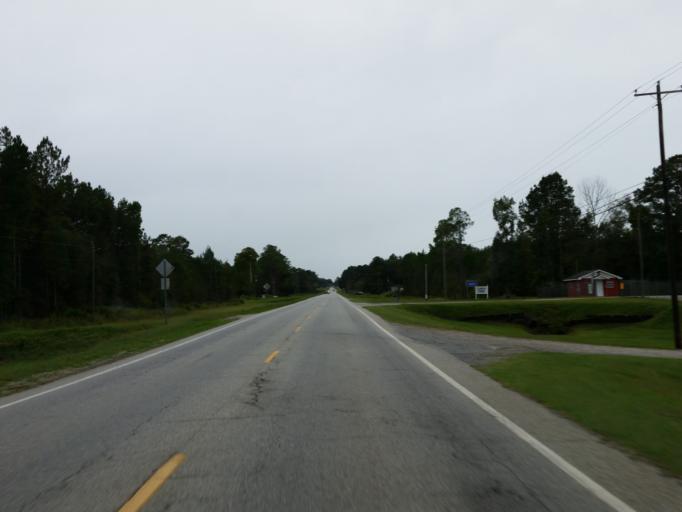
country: US
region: Georgia
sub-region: Lanier County
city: Lakeland
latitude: 31.0447
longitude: -83.0529
